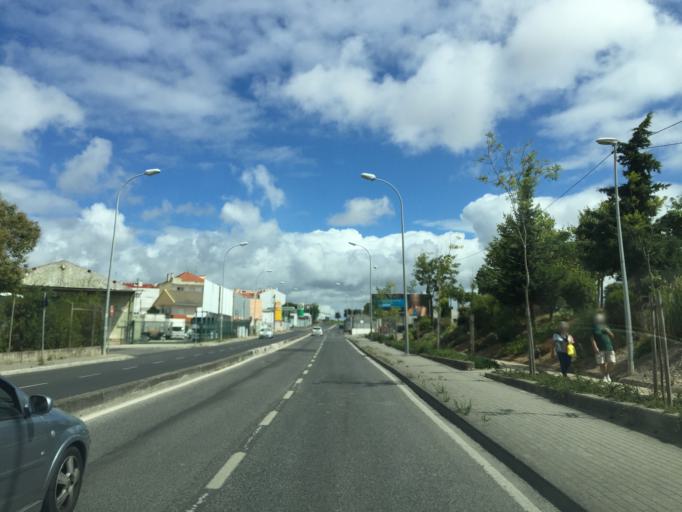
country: PT
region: Lisbon
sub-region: Amadora
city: Amadora
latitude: 38.7753
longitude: -9.2303
